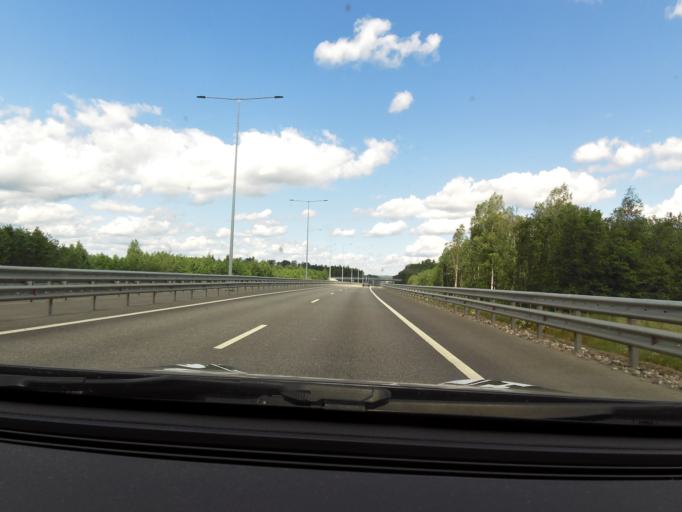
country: RU
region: Tverskaya
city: Vydropuzhsk
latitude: 57.2923
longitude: 34.7806
